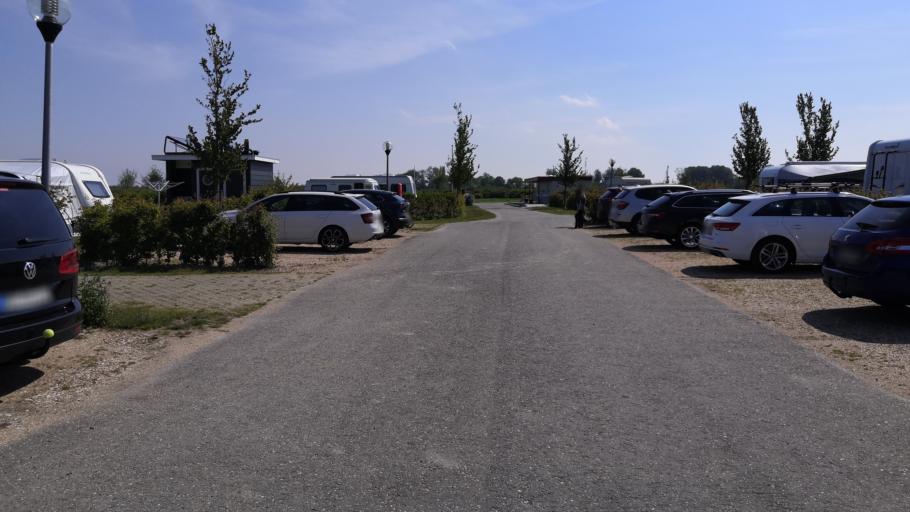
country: NL
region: Zeeland
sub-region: Gemeente Middelburg
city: Middelburg
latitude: 51.5574
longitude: 3.5144
